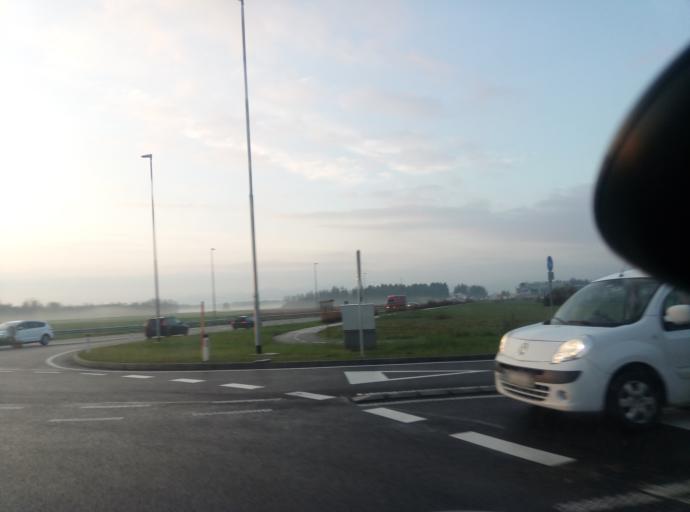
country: SI
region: Kranj
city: Britof
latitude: 46.2420
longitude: 14.3792
